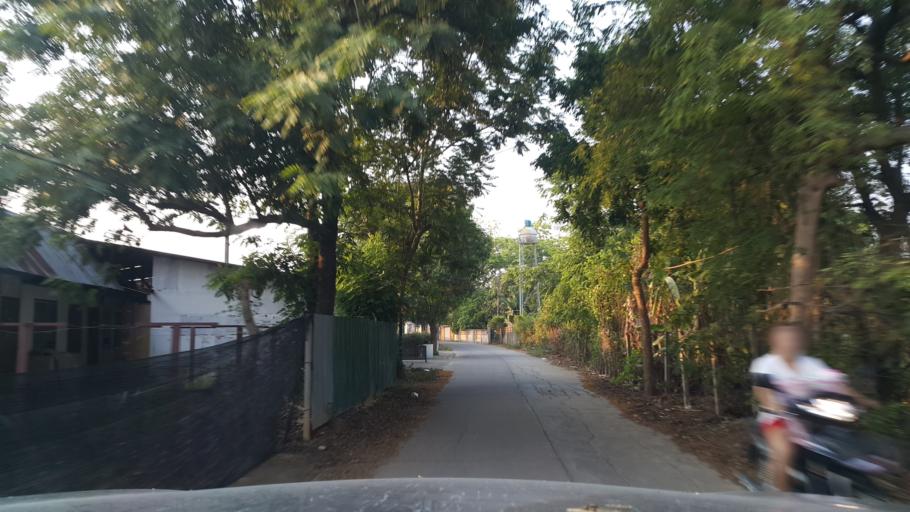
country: TH
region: Chiang Mai
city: Saraphi
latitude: 18.7242
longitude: 99.0173
